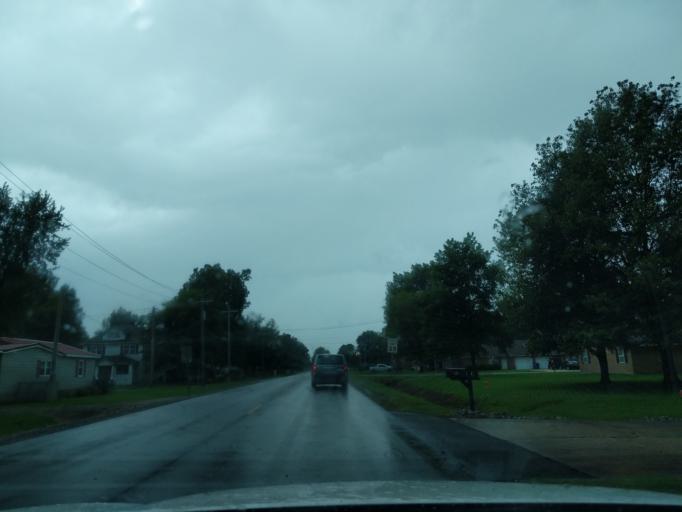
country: US
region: Missouri
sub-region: New Madrid County
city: New Madrid
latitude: 36.5959
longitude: -89.5287
